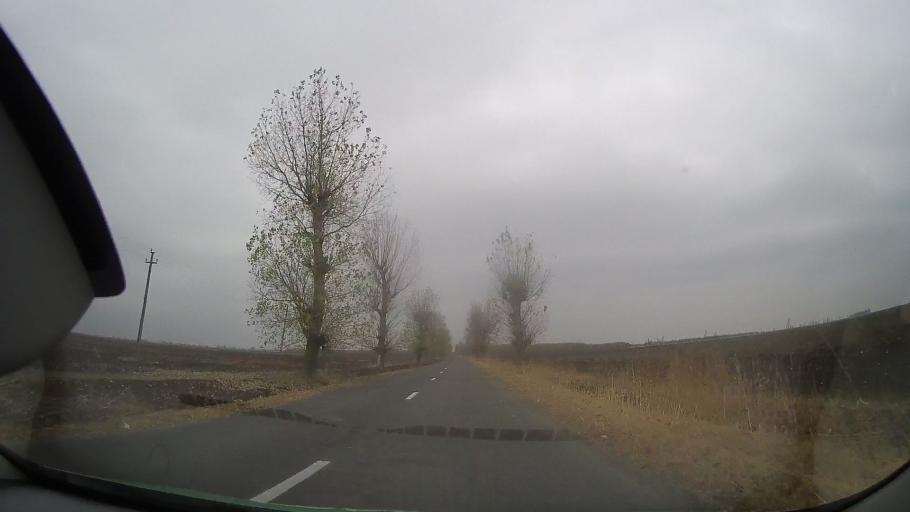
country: RO
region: Ialomita
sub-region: Comuna Grindu
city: Grindu
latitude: 44.7902
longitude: 26.9010
